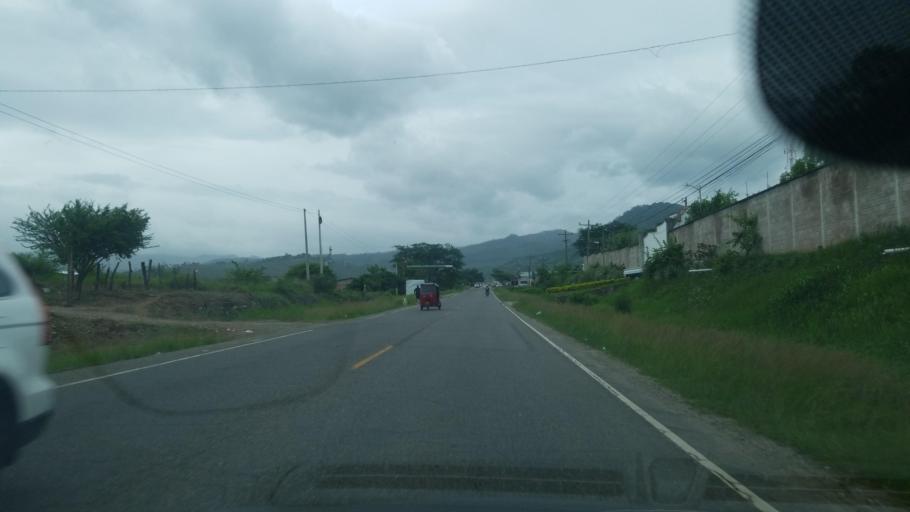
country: HN
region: Ocotepeque
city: Nueva Ocotepeque
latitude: 14.4232
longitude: -89.1864
